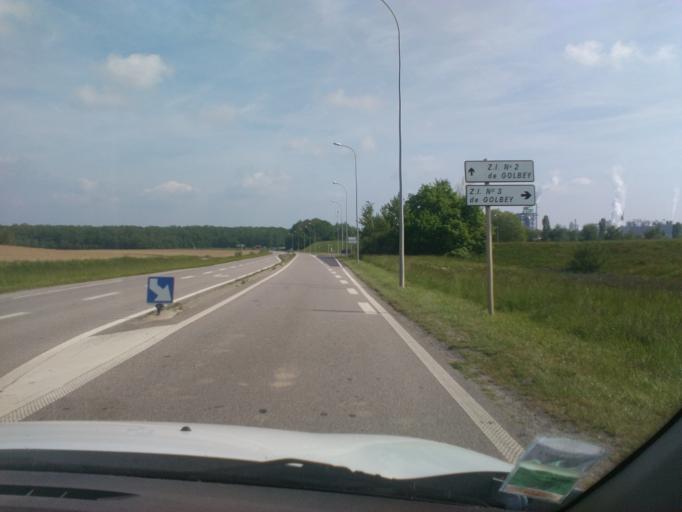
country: FR
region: Lorraine
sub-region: Departement des Vosges
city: Golbey
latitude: 48.2059
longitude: 6.4187
